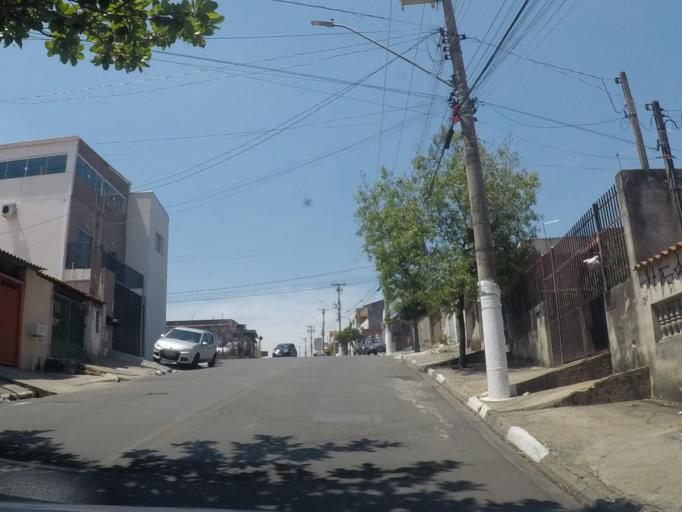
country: BR
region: Sao Paulo
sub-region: Hortolandia
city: Hortolandia
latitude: -22.8570
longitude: -47.2061
